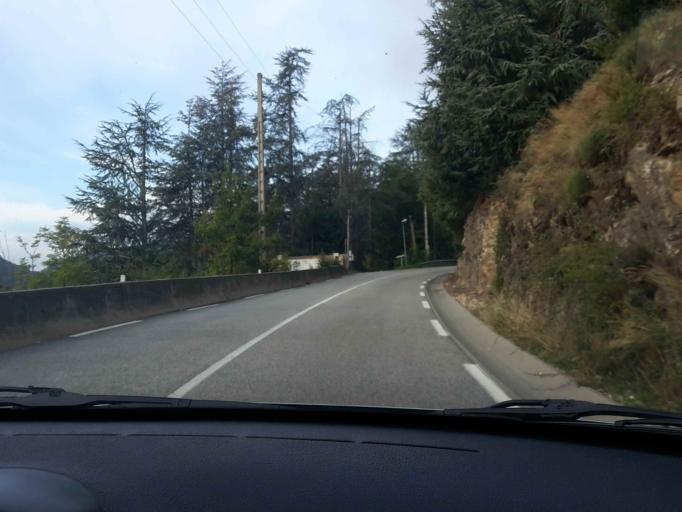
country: FR
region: Rhone-Alpes
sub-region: Departement de la Loire
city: Saint-Paul-en-Cornillon
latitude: 45.4056
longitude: 4.2397
